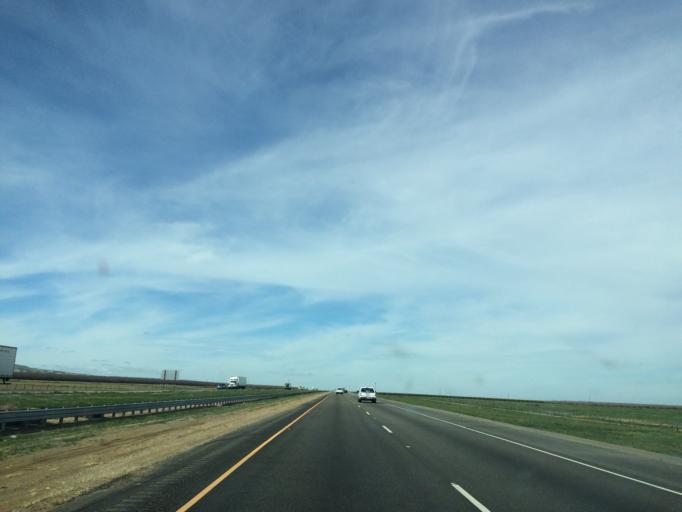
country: US
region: California
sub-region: Merced County
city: South Dos Palos
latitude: 36.6995
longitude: -120.6686
